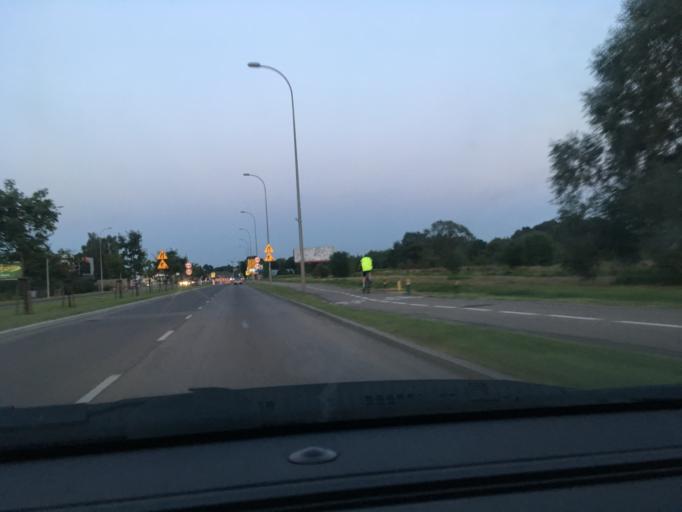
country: PL
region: Podlasie
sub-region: Bialystok
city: Bialystok
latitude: 53.1224
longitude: 23.1896
